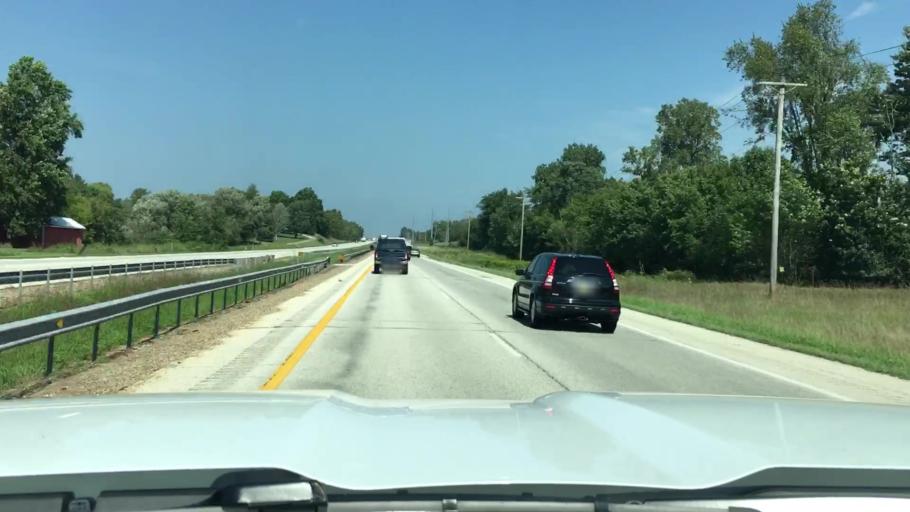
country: US
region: Michigan
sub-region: Kalamazoo County
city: Schoolcraft
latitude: 42.0543
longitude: -85.6357
